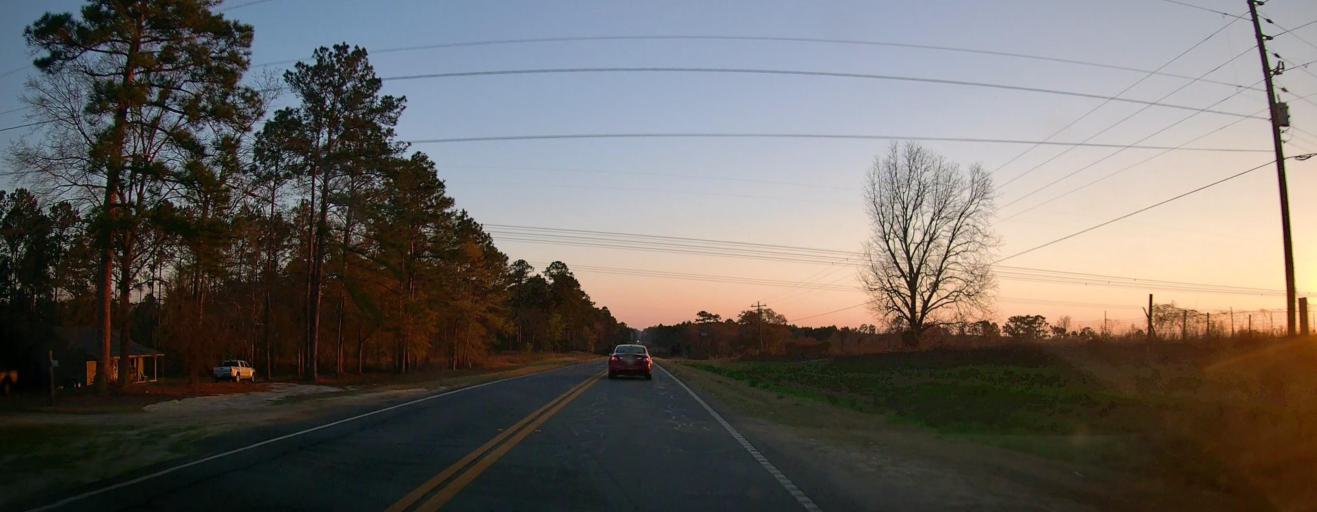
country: US
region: Georgia
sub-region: Dodge County
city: Eastman
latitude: 32.2500
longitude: -83.1424
